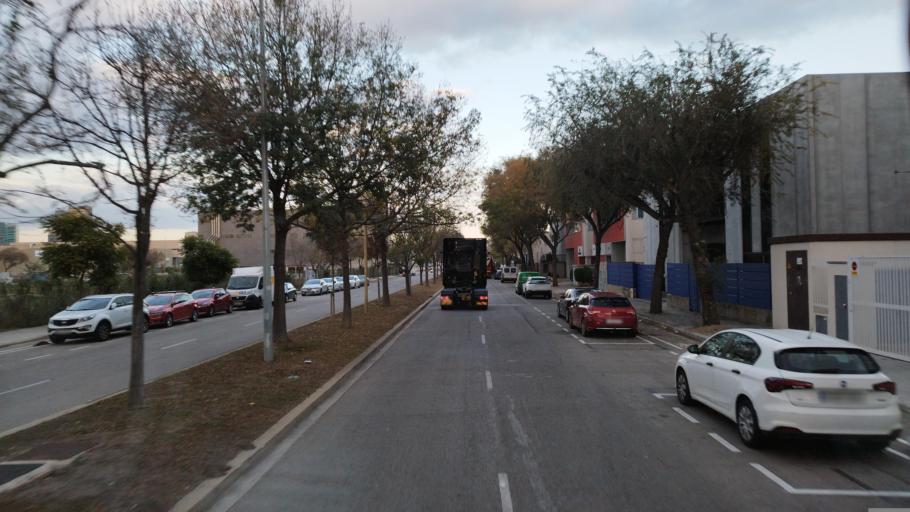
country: ES
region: Catalonia
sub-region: Provincia de Barcelona
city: L'Hospitalet de Llobregat
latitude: 41.3470
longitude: 2.1222
